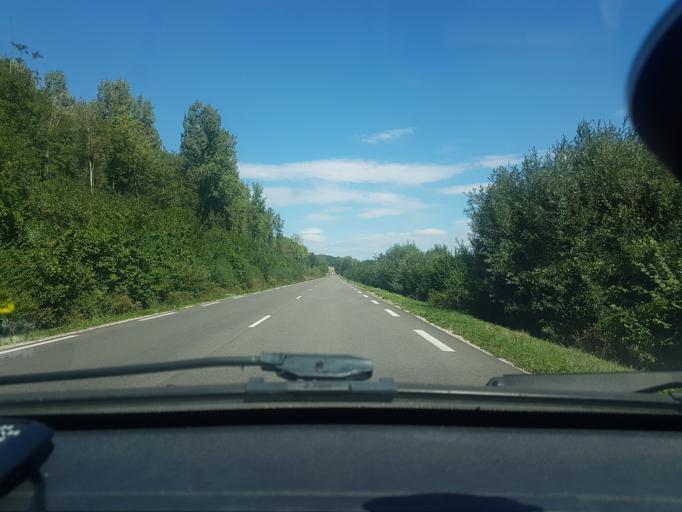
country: FR
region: Franche-Comte
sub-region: Departement de la Haute-Saone
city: Gray-la-Ville
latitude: 47.4367
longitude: 5.5428
